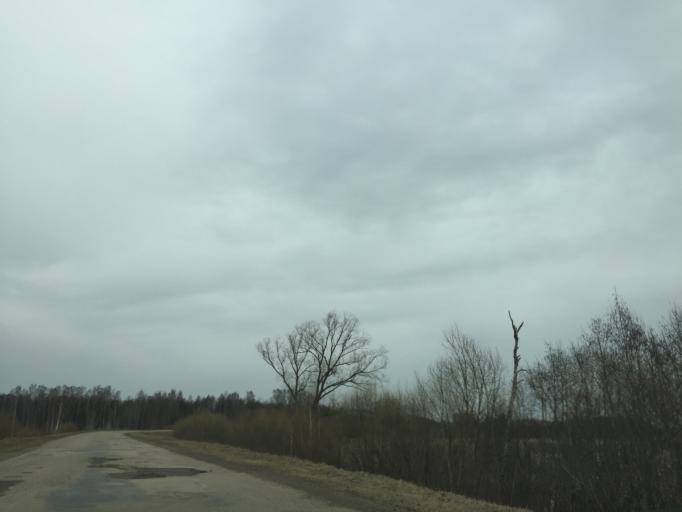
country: LV
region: Ilukste
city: Ilukste
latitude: 56.0444
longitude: 26.2789
